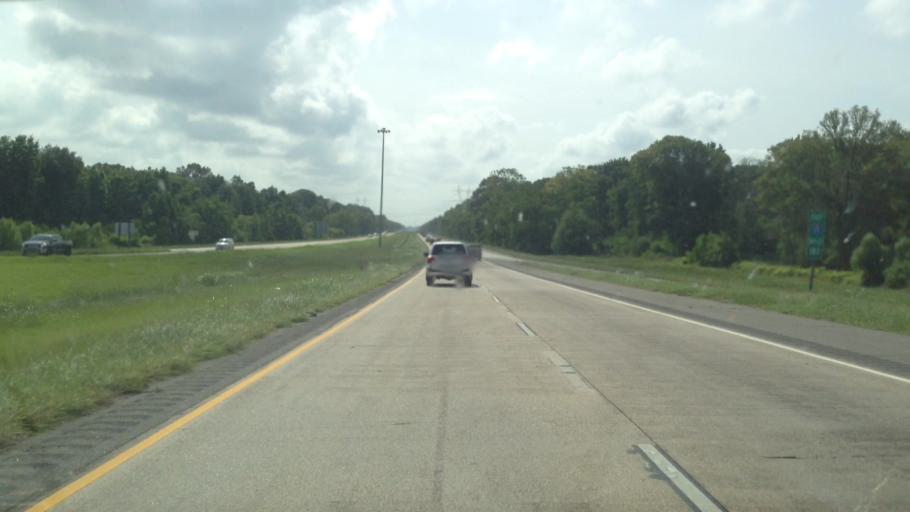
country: US
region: Louisiana
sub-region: Ascension Parish
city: Sorrento
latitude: 30.1706
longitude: -90.8738
